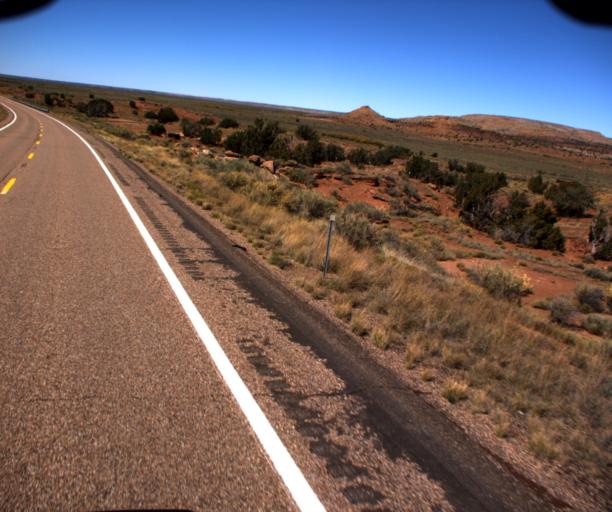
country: US
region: Arizona
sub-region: Apache County
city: Saint Johns
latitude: 34.5856
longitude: -109.5421
